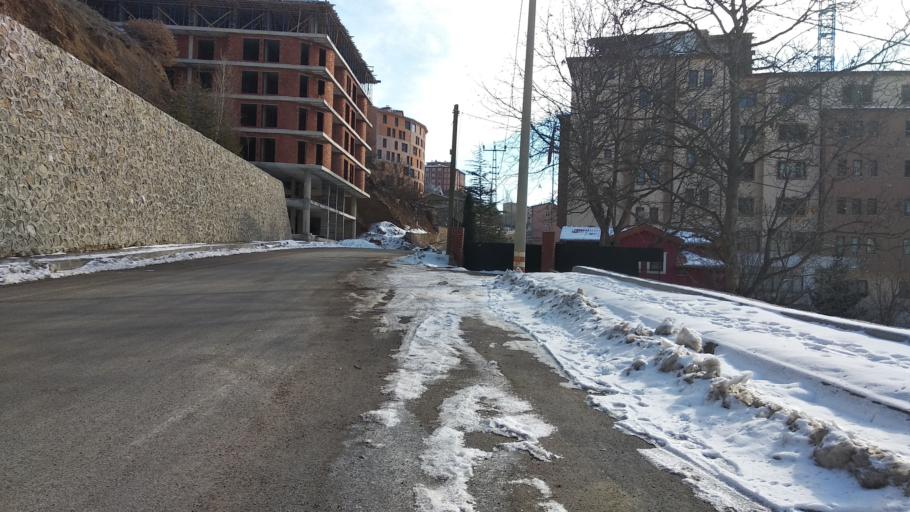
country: TR
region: Gumushane
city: Gumushkhane
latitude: 40.4389
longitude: 39.5056
